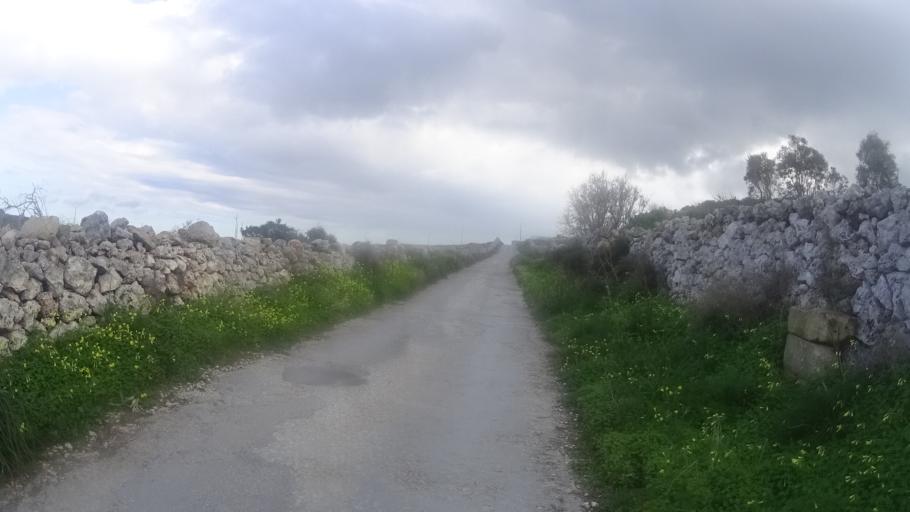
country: MT
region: L-Imgarr
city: Imgarr
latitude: 35.9018
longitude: 14.3698
